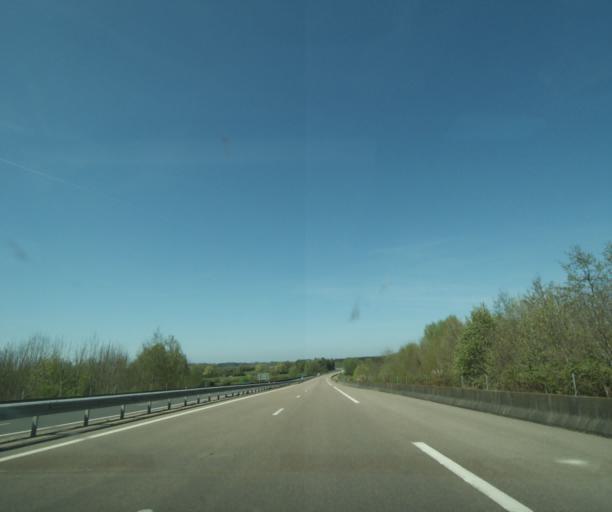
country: FR
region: Bourgogne
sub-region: Departement de la Nievre
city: Pougues-les-Eaux
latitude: 47.0869
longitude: 3.1064
